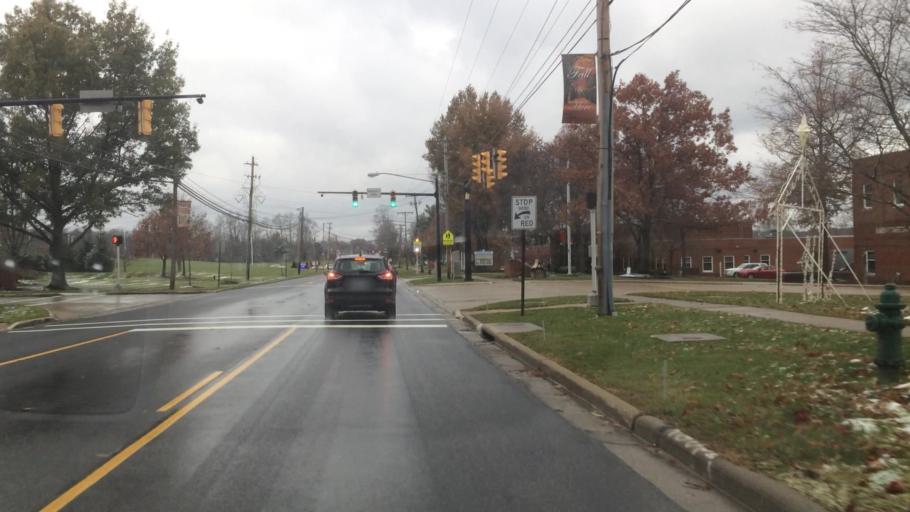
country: US
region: Ohio
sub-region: Summit County
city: Twinsburg
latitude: 41.3174
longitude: -81.4475
